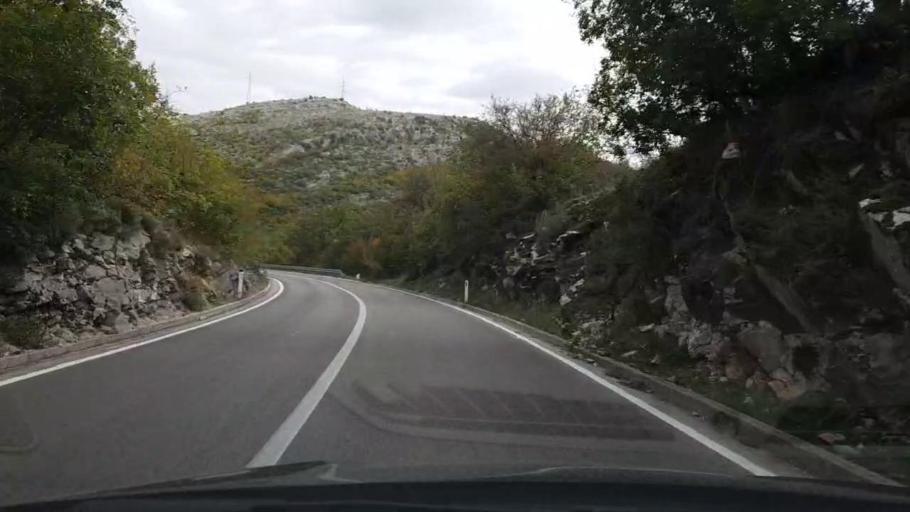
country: BA
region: Republika Srpska
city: Trebinje
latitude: 42.6814
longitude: 18.2983
